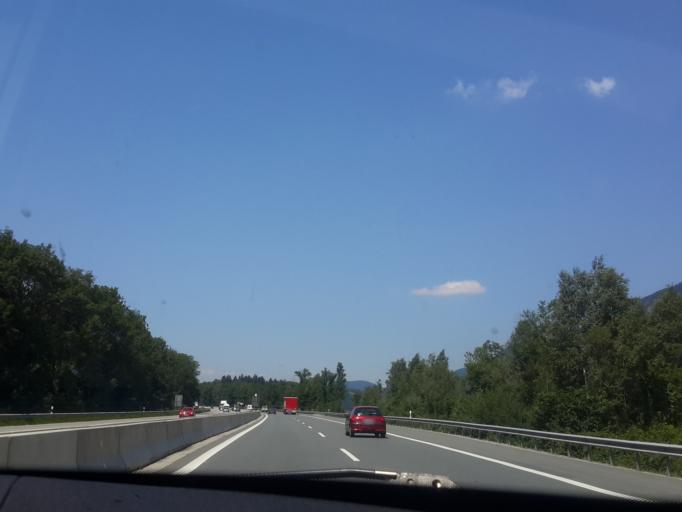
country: AT
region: Tyrol
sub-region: Politischer Bezirk Kufstein
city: Erl
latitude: 47.6948
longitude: 12.1624
